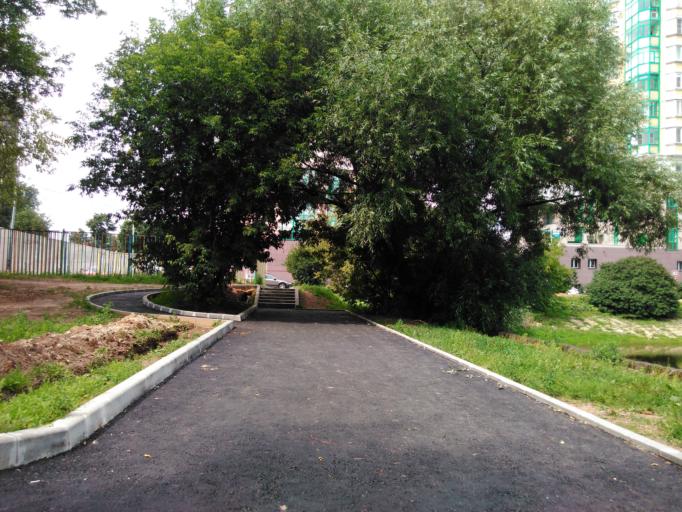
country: RU
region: Moscow
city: Ramenki
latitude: 55.6774
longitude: 37.5115
